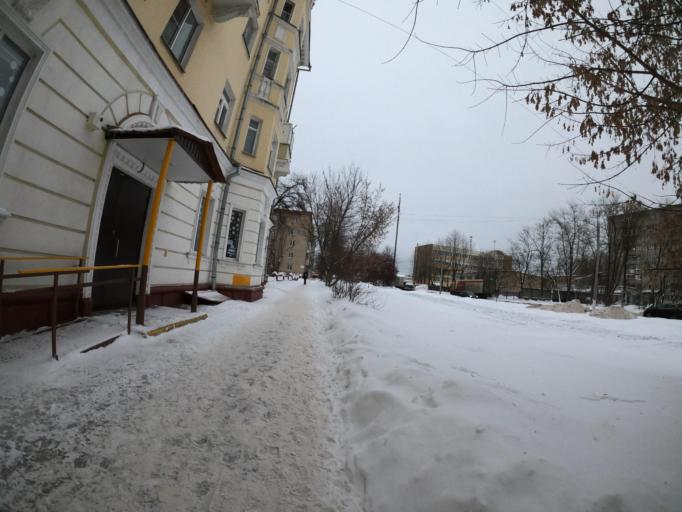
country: RU
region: Moskovskaya
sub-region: Podol'skiy Rayon
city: Podol'sk
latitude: 55.4143
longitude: 37.5453
